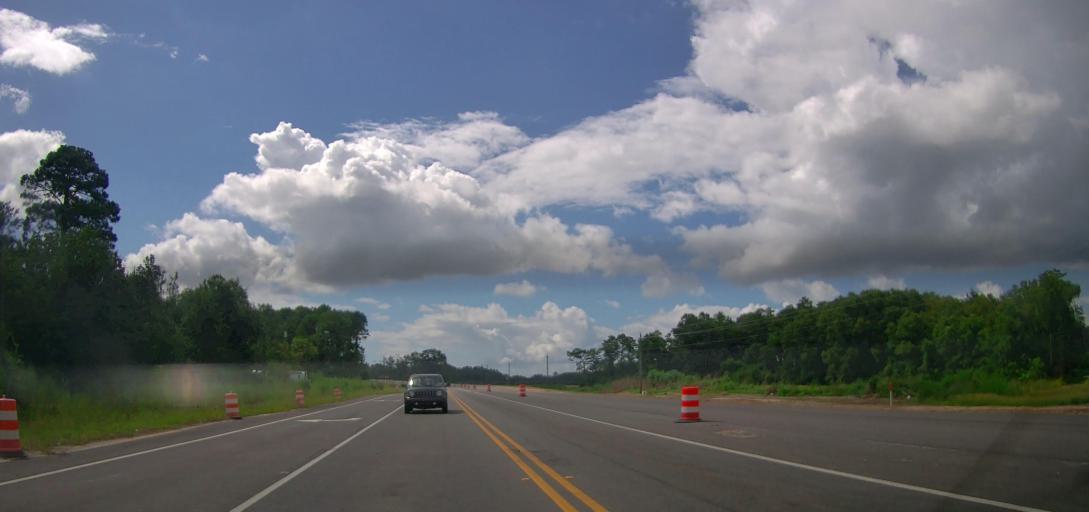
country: US
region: Georgia
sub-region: Coffee County
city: Broxton
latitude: 31.5462
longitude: -82.9353
